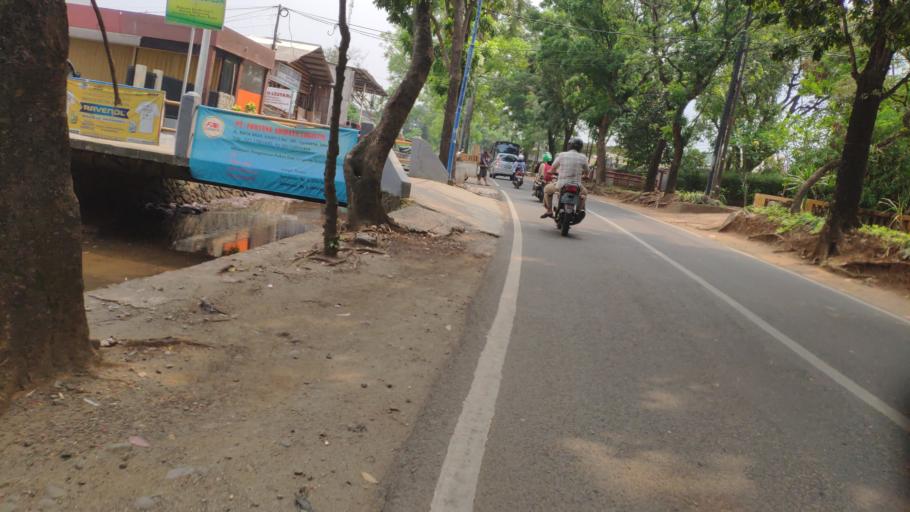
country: ID
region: West Java
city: Depok
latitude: -6.3473
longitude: 106.8139
